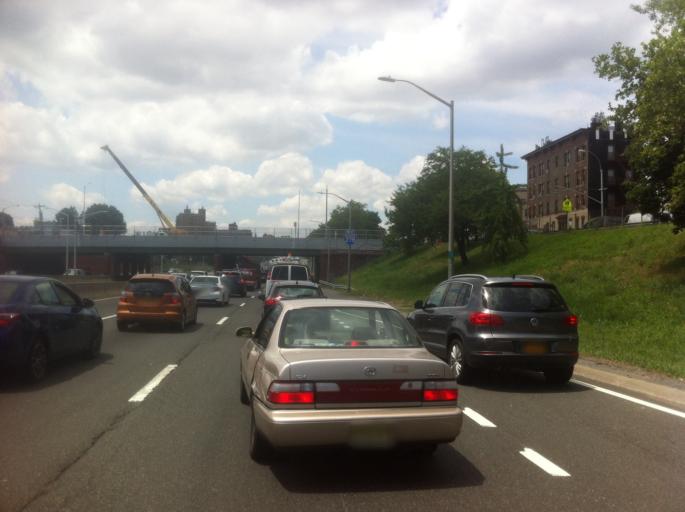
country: US
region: New York
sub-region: Bronx
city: The Bronx
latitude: 40.8275
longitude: -73.8486
